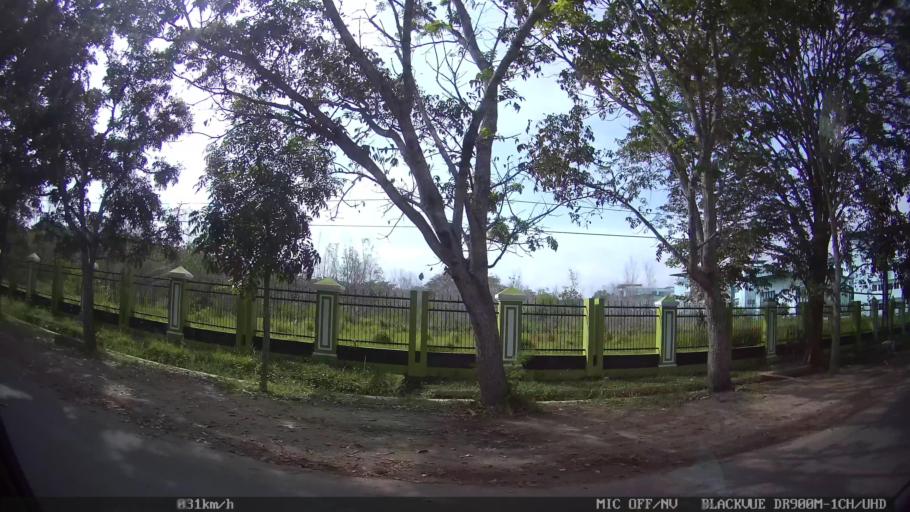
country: ID
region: Lampung
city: Kedaton
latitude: -5.3772
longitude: 105.3052
